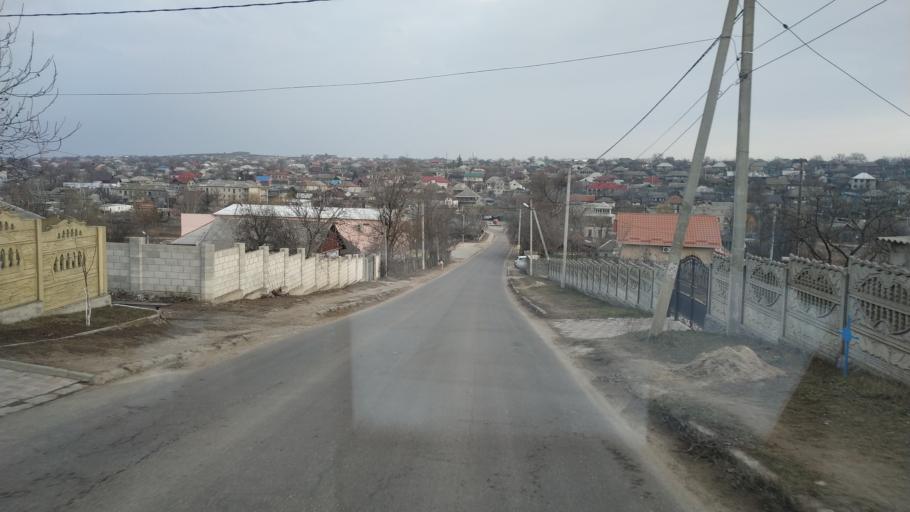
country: MD
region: Chisinau
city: Singera
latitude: 46.9578
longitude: 29.0604
